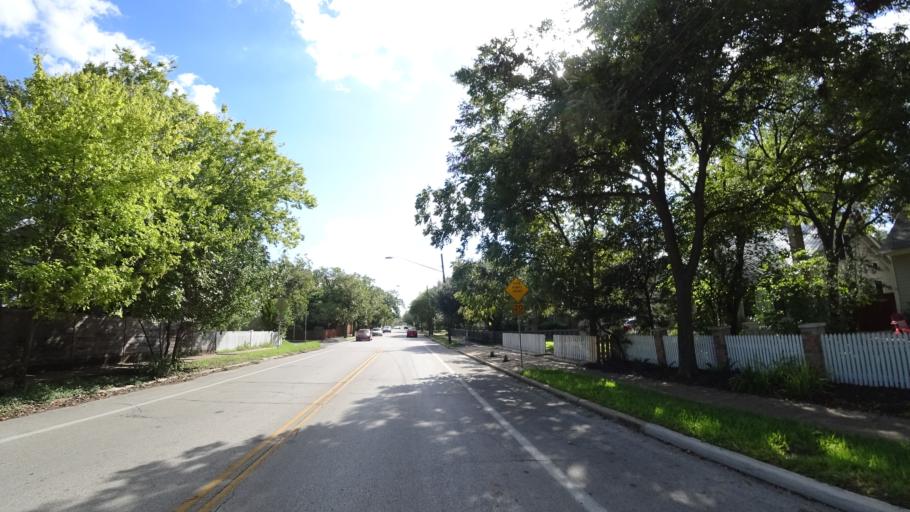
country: US
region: Texas
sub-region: Travis County
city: Austin
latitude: 30.3026
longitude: -97.7274
